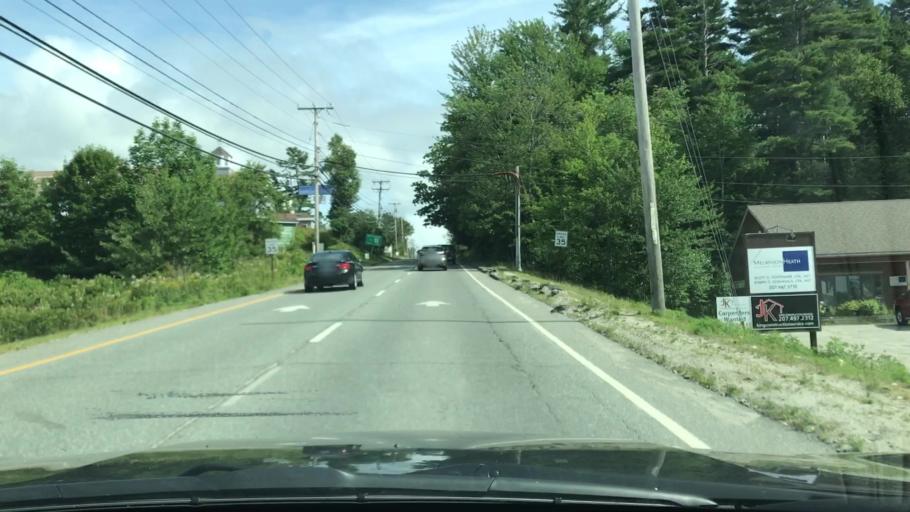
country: US
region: Maine
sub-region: Hancock County
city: Ellsworth
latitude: 44.5296
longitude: -68.4047
